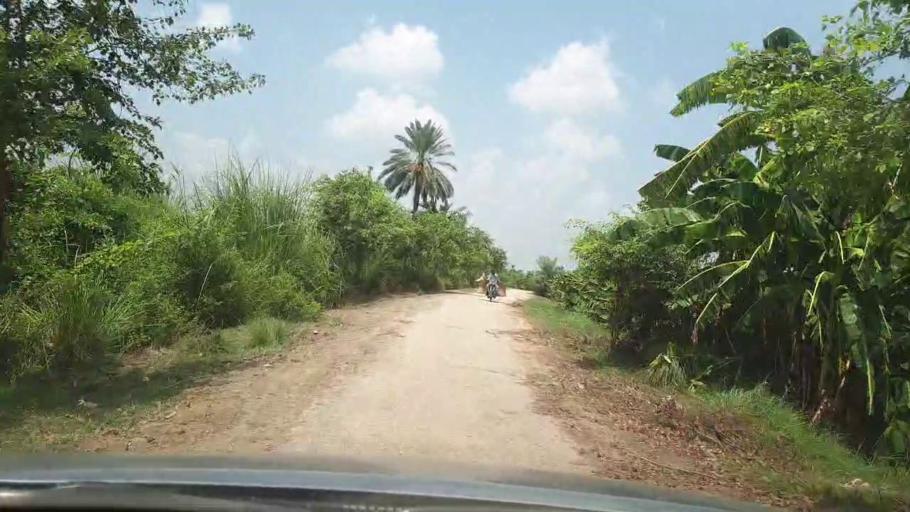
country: PK
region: Sindh
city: Pir jo Goth
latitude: 27.6046
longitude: 68.6121
